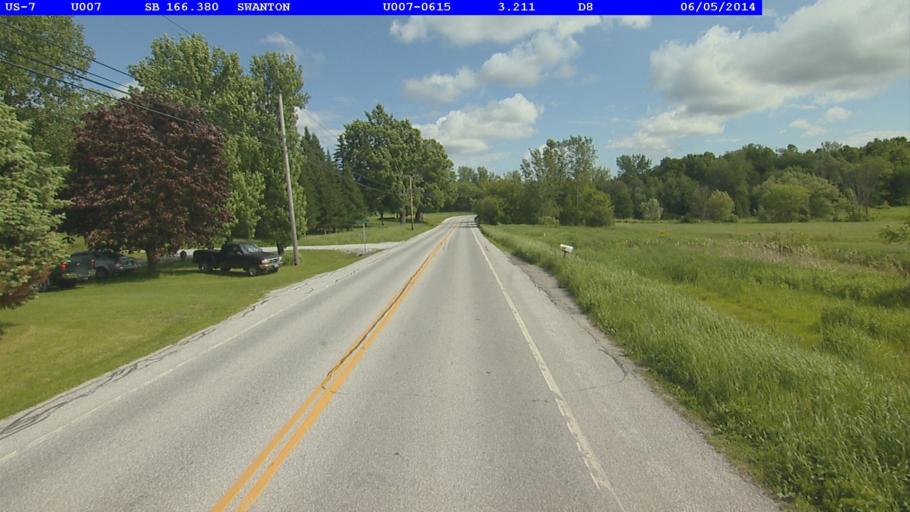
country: US
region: Vermont
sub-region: Franklin County
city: Swanton
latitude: 44.8924
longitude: -73.0914
